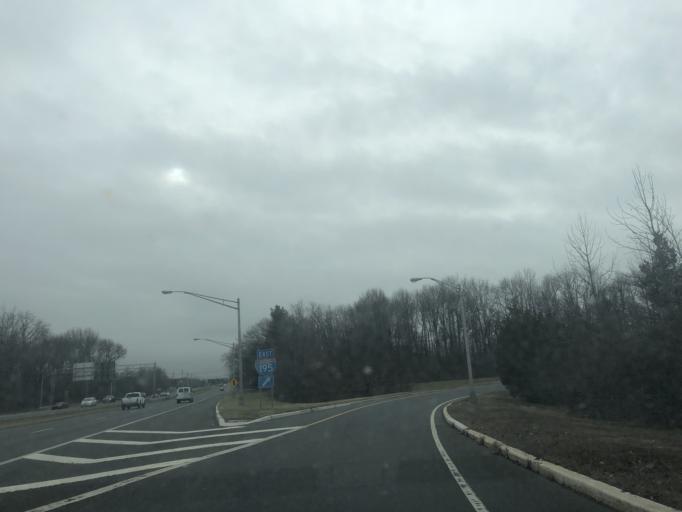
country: US
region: New Jersey
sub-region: Mercer County
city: Robbinsville
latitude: 40.2017
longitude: -74.6363
